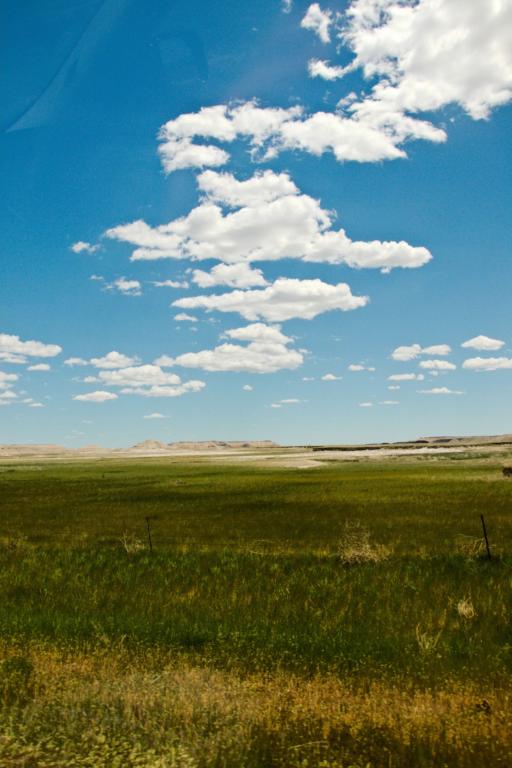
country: US
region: South Dakota
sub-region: Shannon County
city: Porcupine
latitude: 43.7885
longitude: -102.5292
